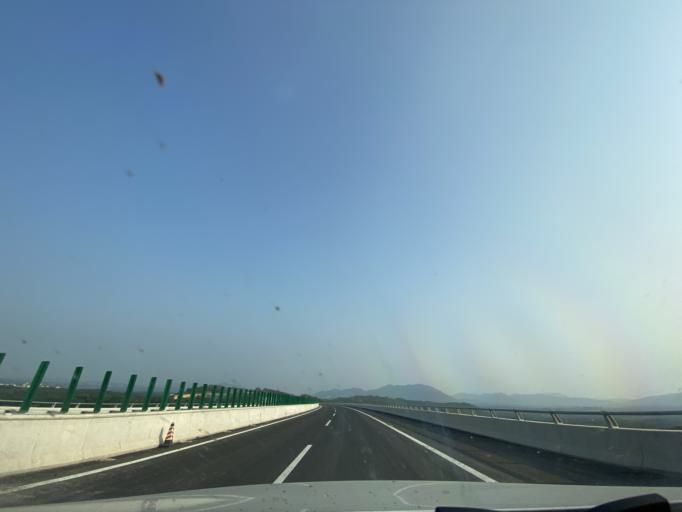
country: CN
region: Hainan
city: Xiangshui
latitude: 18.6371
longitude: 109.6302
